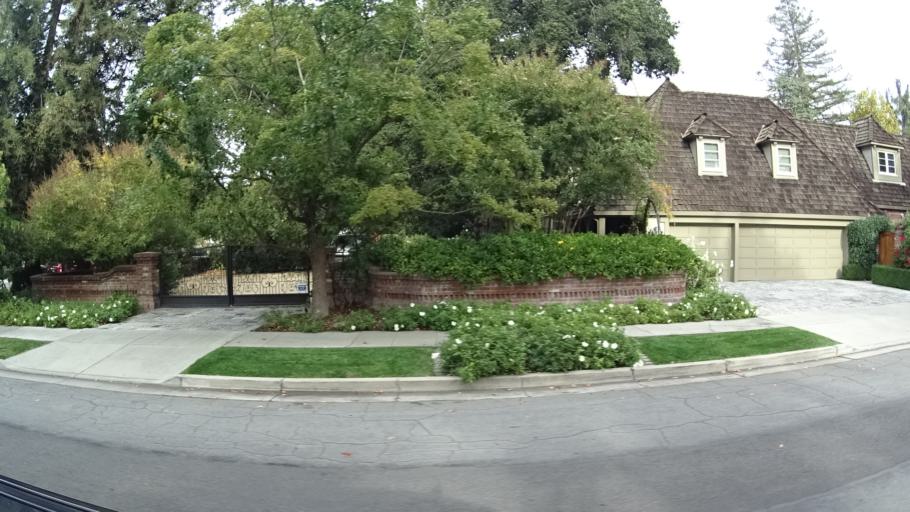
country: US
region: California
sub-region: Santa Clara County
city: Burbank
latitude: 37.3339
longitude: -121.9293
